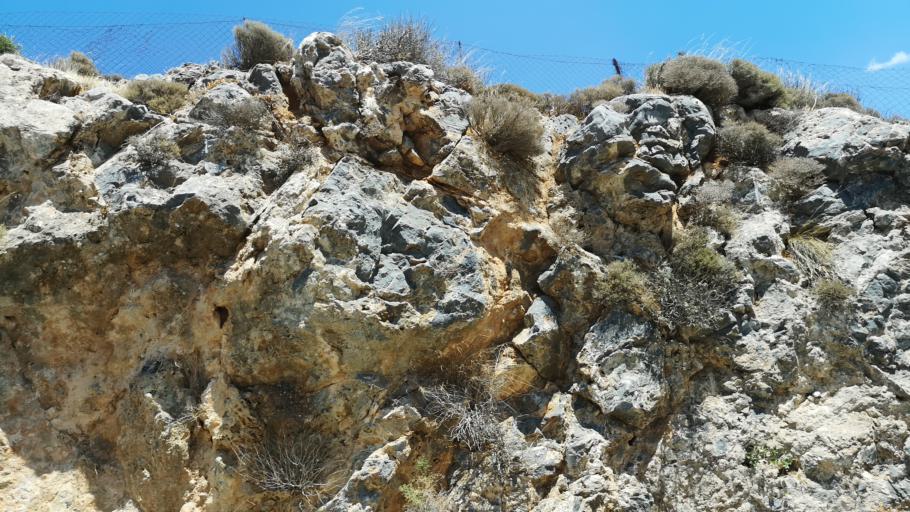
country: GR
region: Crete
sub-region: Nomos Lasithiou
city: Neapoli
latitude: 35.2508
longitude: 25.6320
